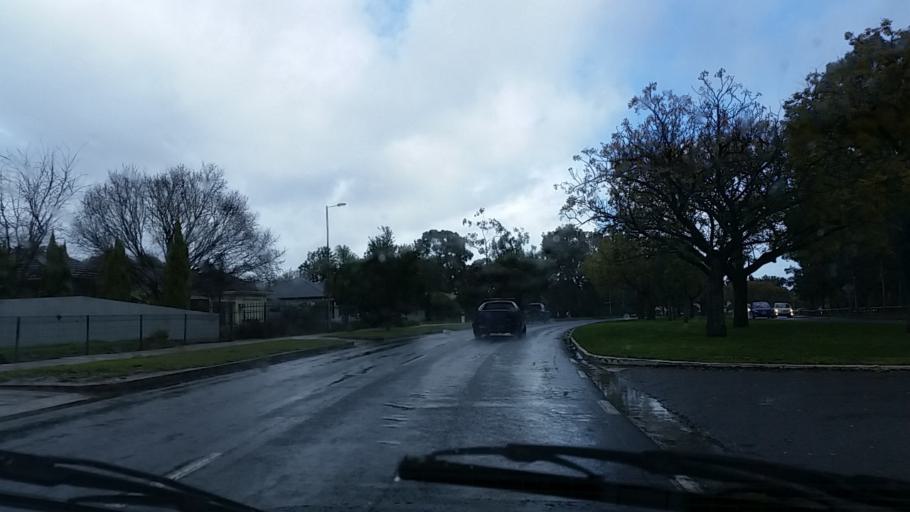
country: AU
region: South Australia
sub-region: Salisbury
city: Elizabeth
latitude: -34.7172
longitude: 138.6799
